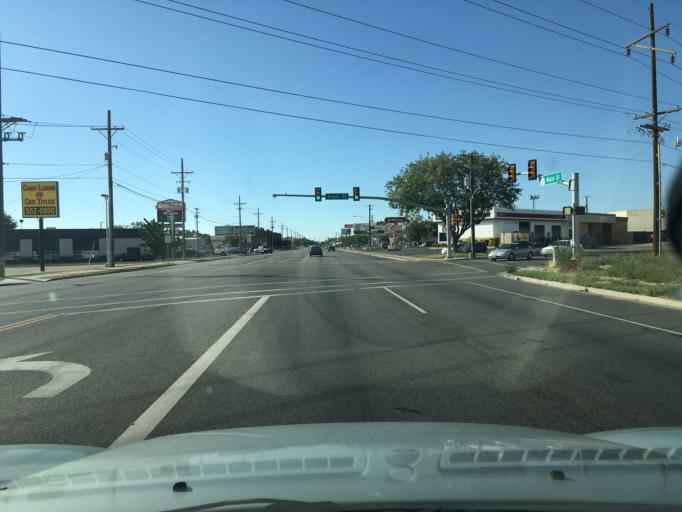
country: US
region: Utah
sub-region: Davis County
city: Layton
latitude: 41.0792
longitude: -111.9876
